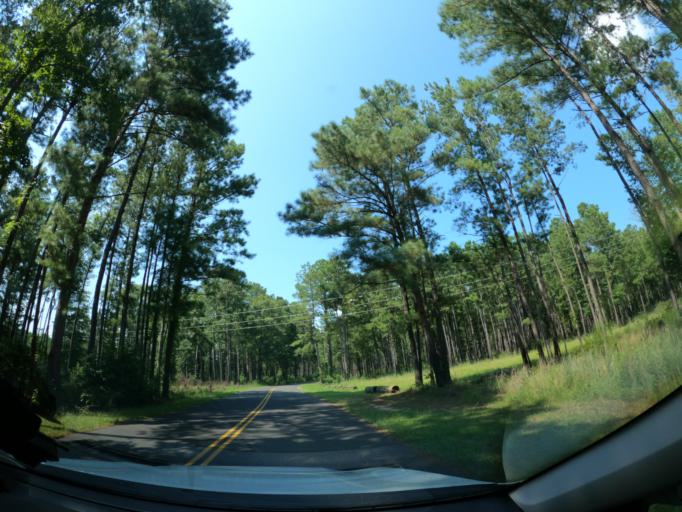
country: US
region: South Carolina
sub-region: Richland County
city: Gadsden
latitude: 33.8392
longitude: -80.8286
